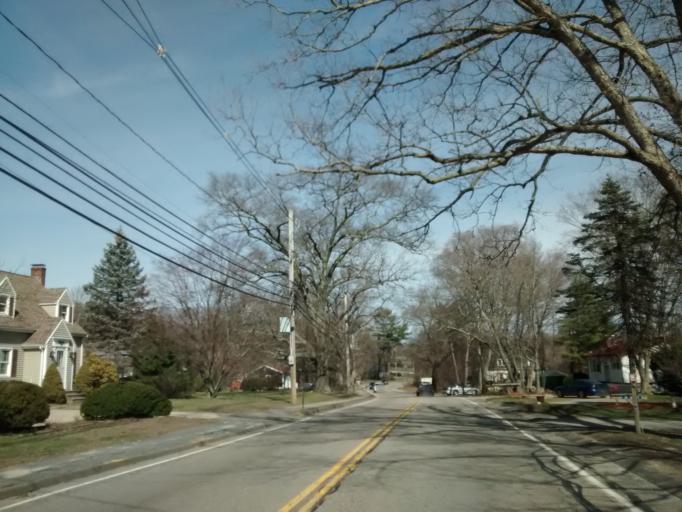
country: US
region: Massachusetts
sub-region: Norfolk County
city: Bellingham
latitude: 42.1129
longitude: -71.4772
